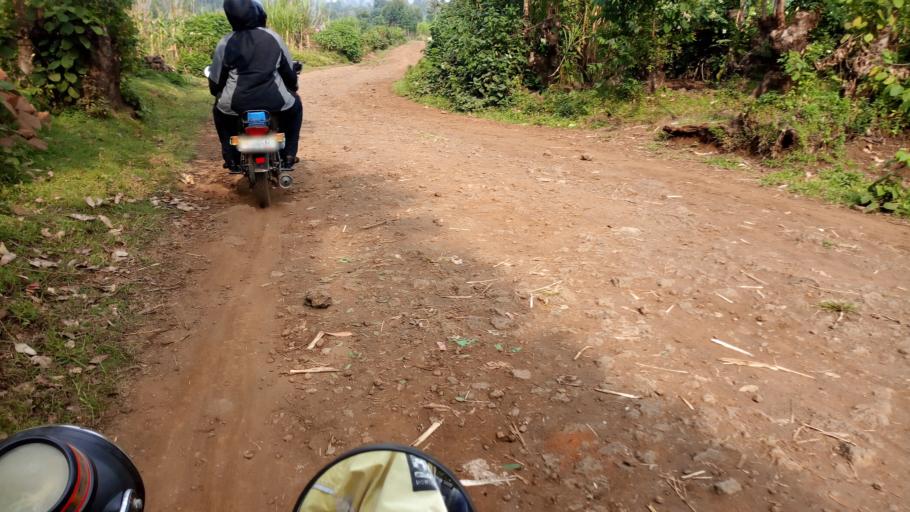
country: UG
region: Western Region
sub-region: Kisoro District
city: Kisoro
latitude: -1.3111
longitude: 29.6546
